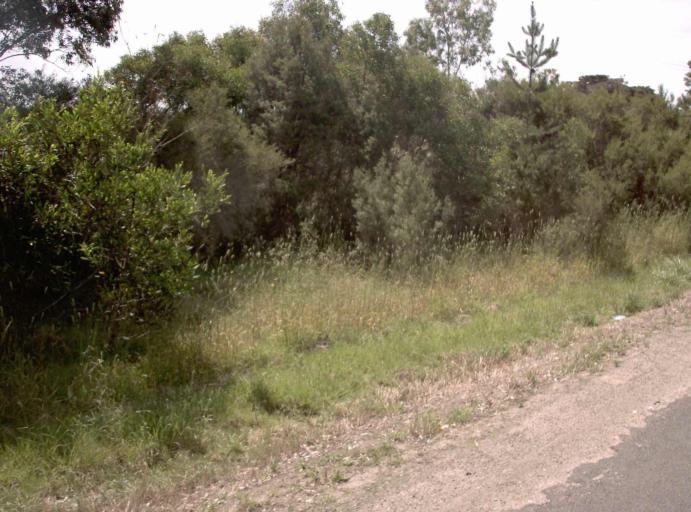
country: AU
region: Victoria
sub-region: Wellington
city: Sale
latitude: -38.0765
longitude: 147.0723
